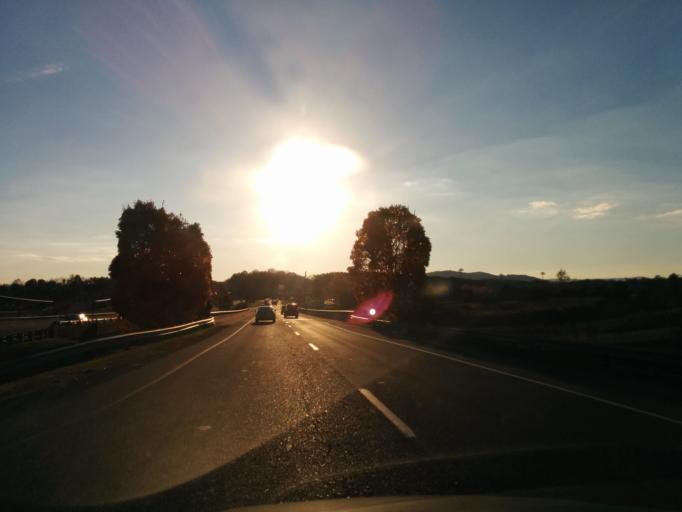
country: US
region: Virginia
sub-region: Rockbridge County
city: East Lexington
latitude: 37.8016
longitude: -79.4135
